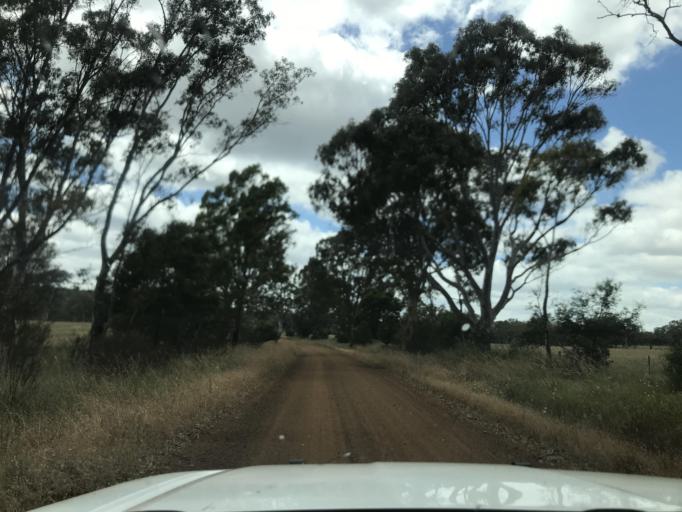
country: AU
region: South Australia
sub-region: Wattle Range
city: Penola
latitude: -37.3719
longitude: 141.2333
